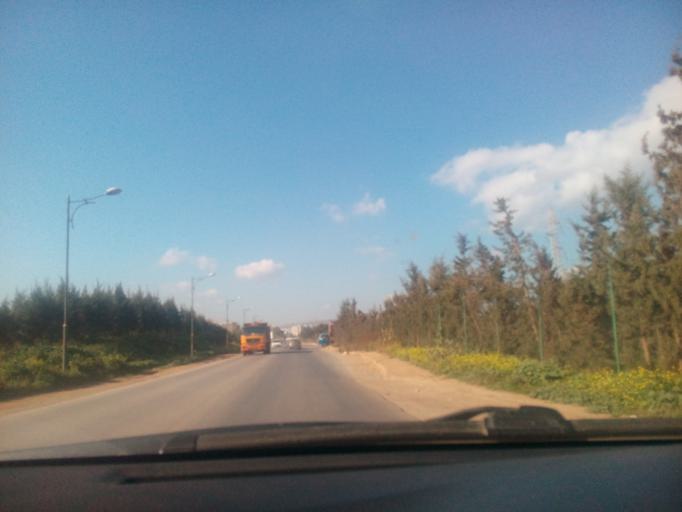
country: DZ
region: Oran
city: Es Senia
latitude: 35.6757
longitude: -0.5914
